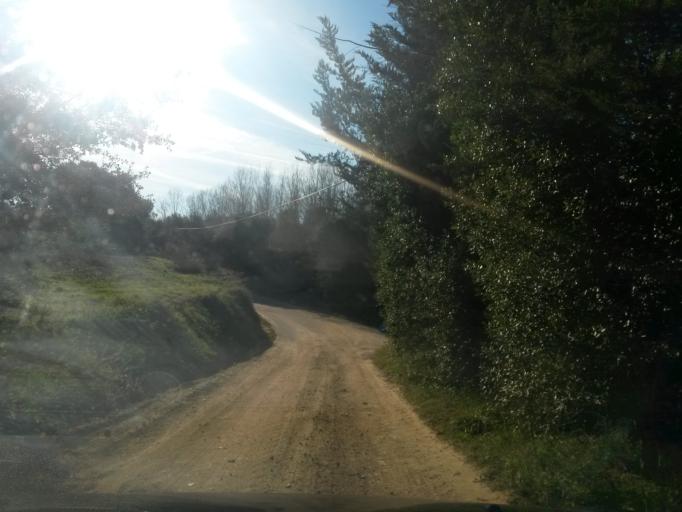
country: ES
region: Catalonia
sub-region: Provincia de Girona
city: la Cellera de Ter
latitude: 41.9702
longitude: 2.6300
